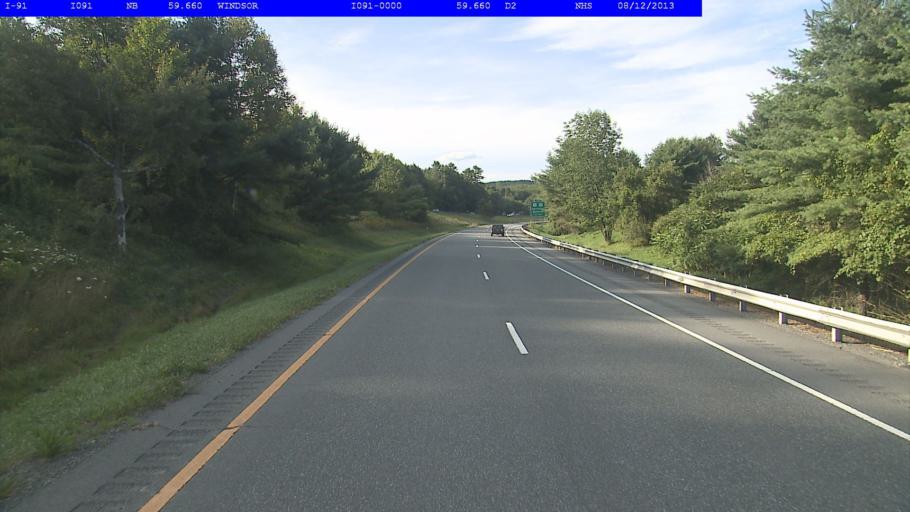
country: US
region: Vermont
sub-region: Windsor County
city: Windsor
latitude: 43.5178
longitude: -72.4083
